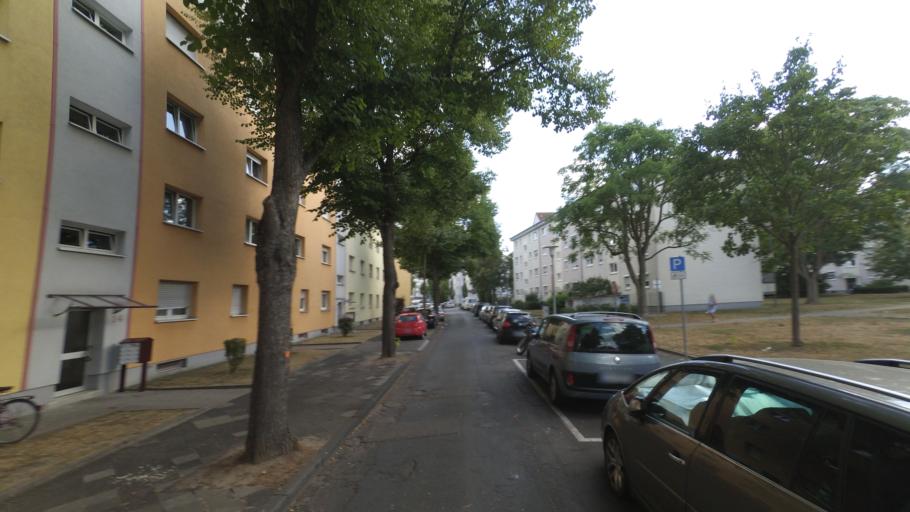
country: DE
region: Baden-Wuerttemberg
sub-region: Karlsruhe Region
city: Mannheim
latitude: 49.5056
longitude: 8.4672
